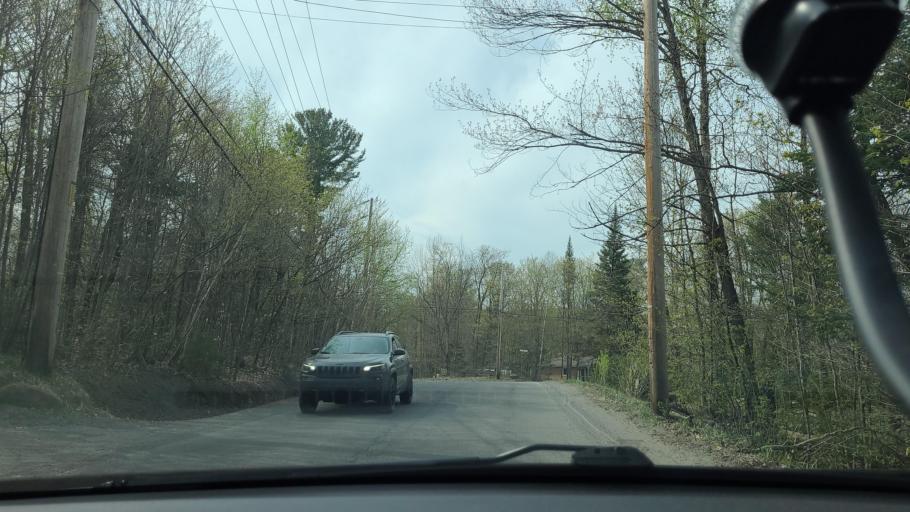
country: CA
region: Quebec
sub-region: Laurentides
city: Prevost
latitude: 45.8918
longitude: -74.0528
